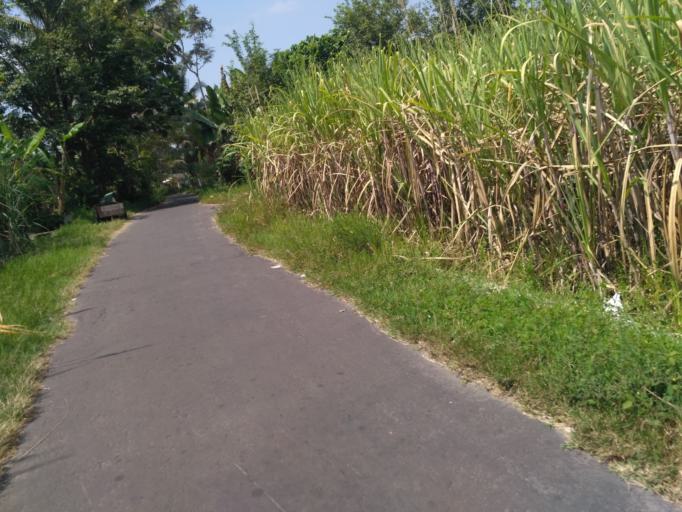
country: ID
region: Daerah Istimewa Yogyakarta
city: Depok
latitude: -7.7109
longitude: 110.4223
